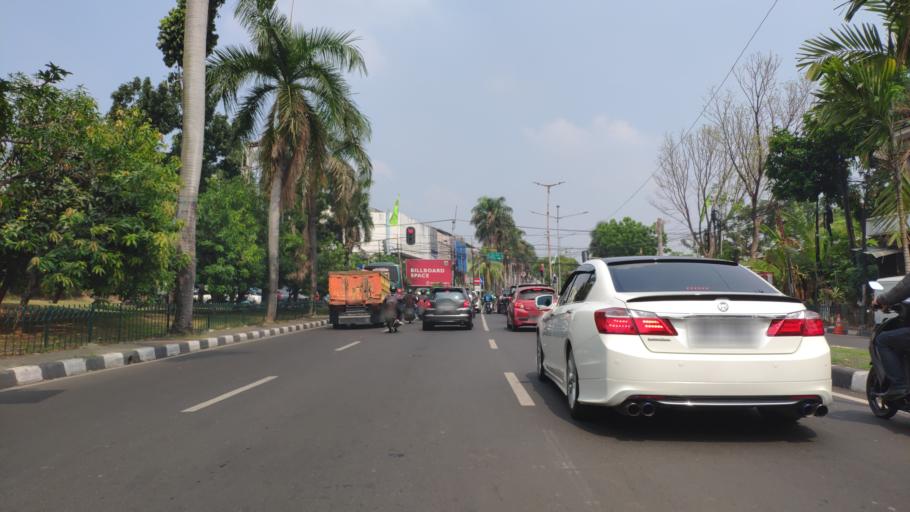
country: ID
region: Banten
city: South Tangerang
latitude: -6.2741
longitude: 106.7748
